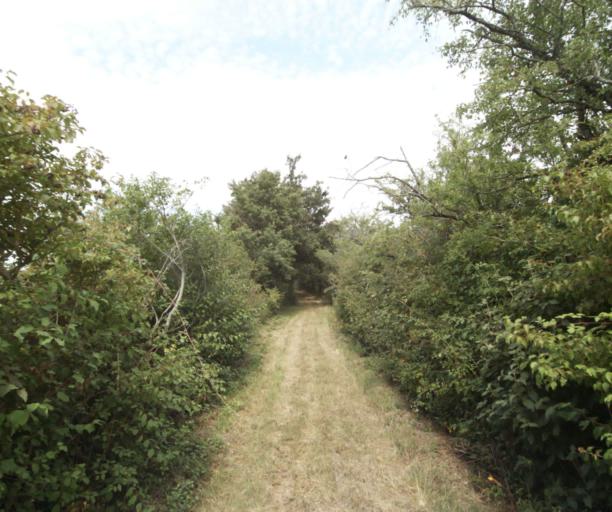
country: FR
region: Midi-Pyrenees
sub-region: Departement de la Haute-Garonne
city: Saint-Felix-Lauragais
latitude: 43.4266
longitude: 1.9260
